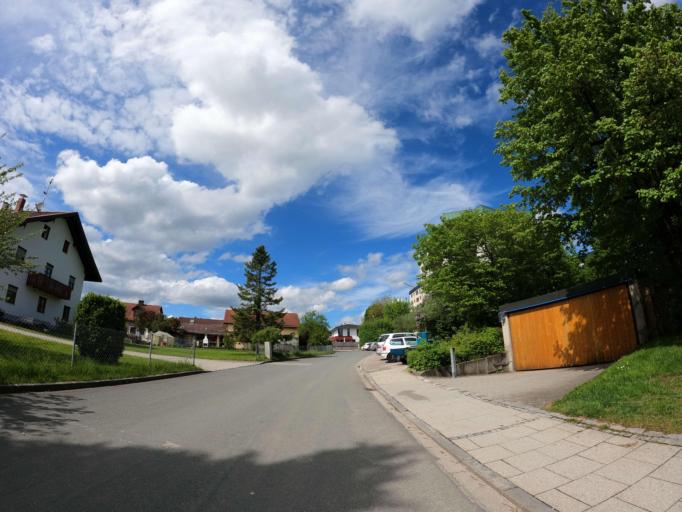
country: DE
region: Bavaria
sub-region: Upper Bavaria
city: Ebersberg
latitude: 48.0734
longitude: 11.9546
